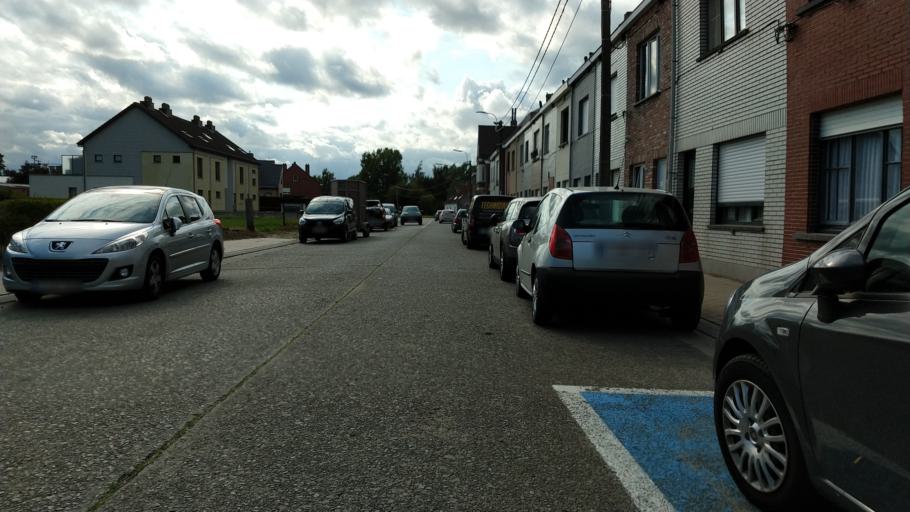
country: BE
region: Flanders
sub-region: Provincie Oost-Vlaanderen
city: Wetteren
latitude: 50.9988
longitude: 3.8579
